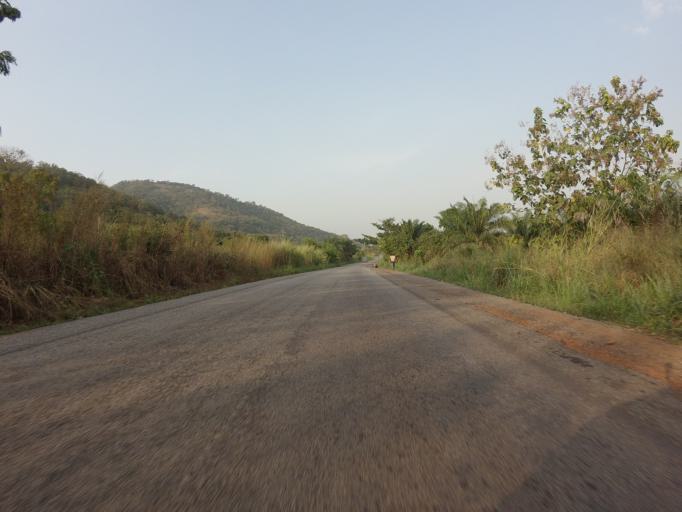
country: GH
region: Volta
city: Ho
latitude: 6.5572
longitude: 0.2957
